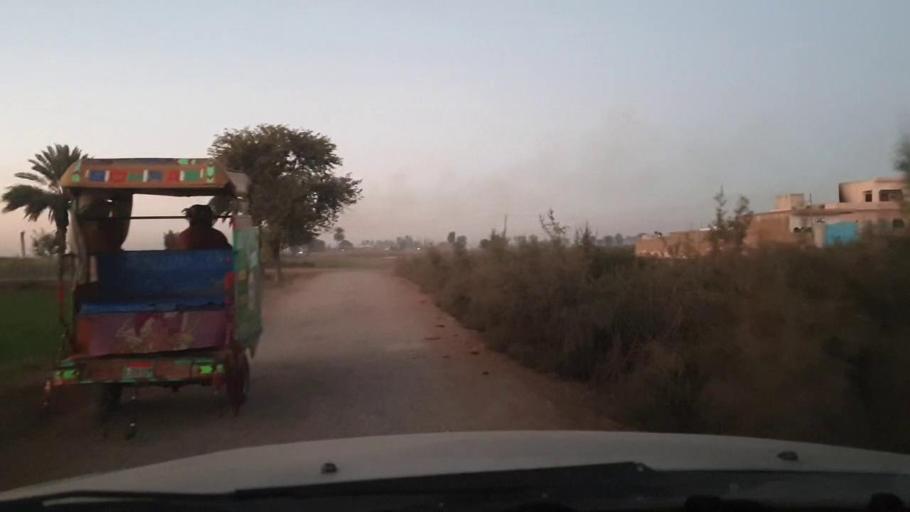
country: PK
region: Sindh
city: Ghotki
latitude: 27.9846
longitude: 69.2870
